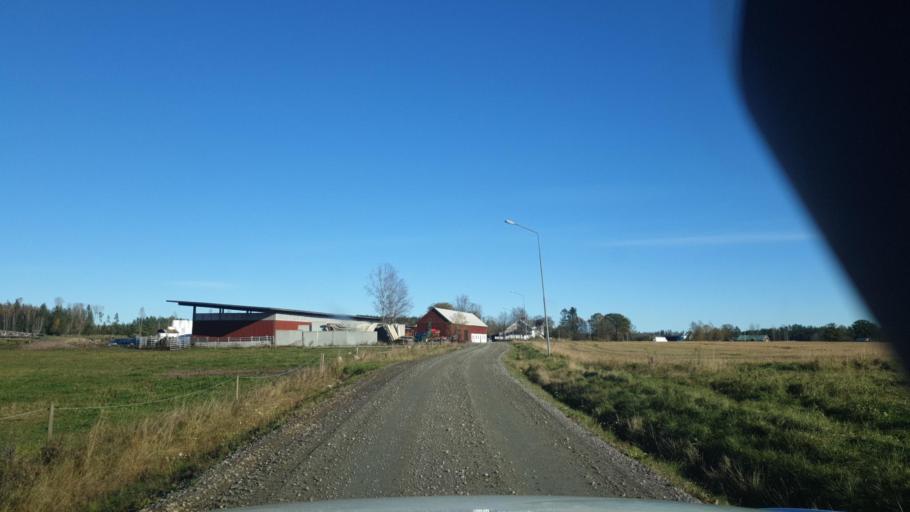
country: SE
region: Vaermland
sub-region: Karlstads Kommun
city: Edsvalla
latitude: 59.4928
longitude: 13.1714
